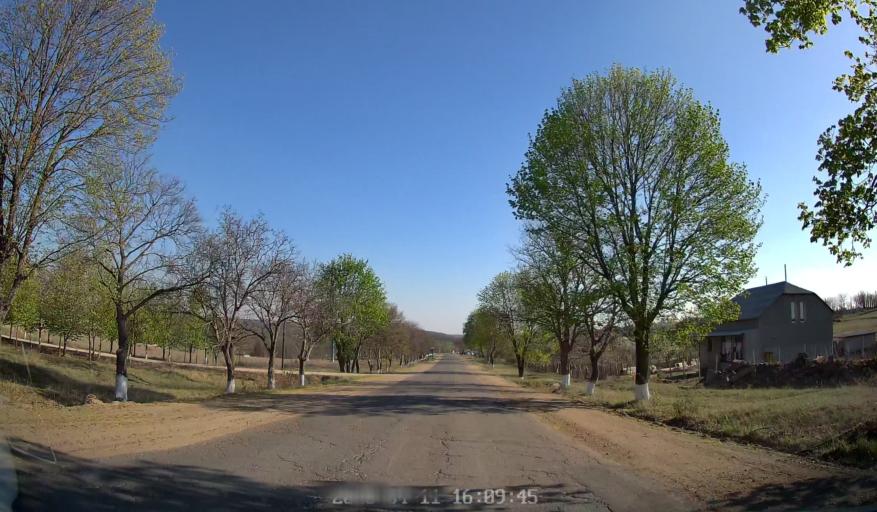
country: MD
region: Chisinau
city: Vadul lui Voda
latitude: 47.0718
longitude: 29.1368
